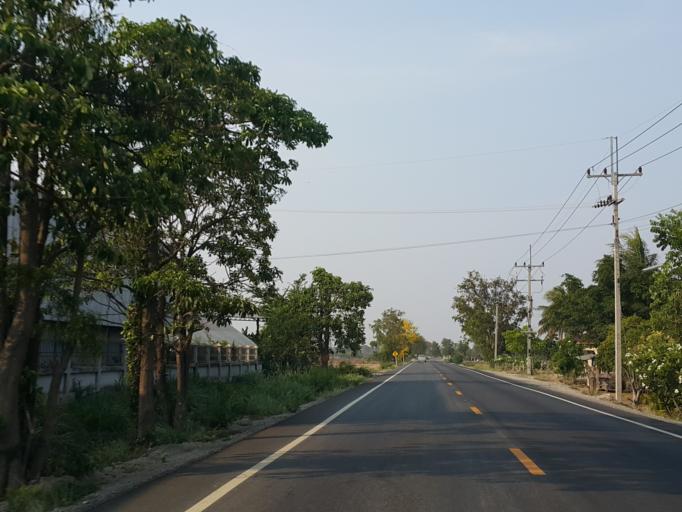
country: TH
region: Chai Nat
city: Hankha
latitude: 14.9557
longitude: 100.0906
